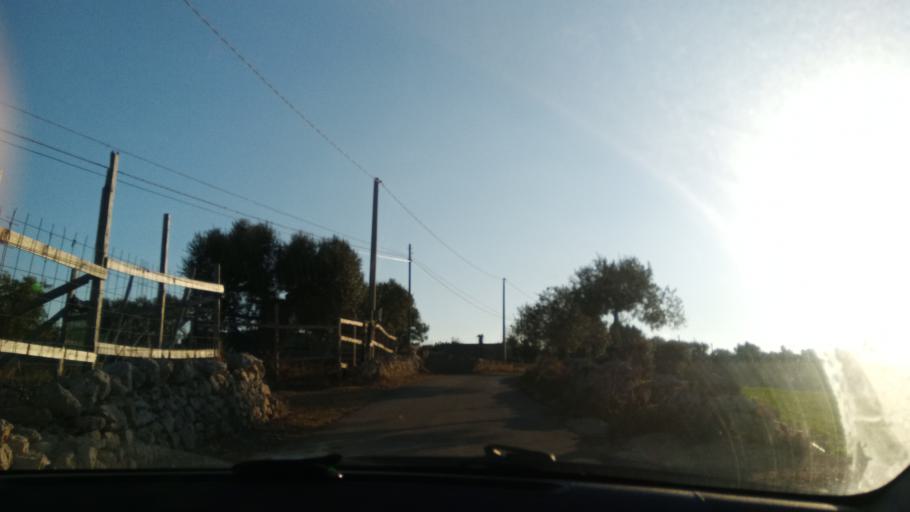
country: IT
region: Apulia
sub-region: Provincia di Bari
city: Polignano a Mare
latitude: 40.9817
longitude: 17.2085
